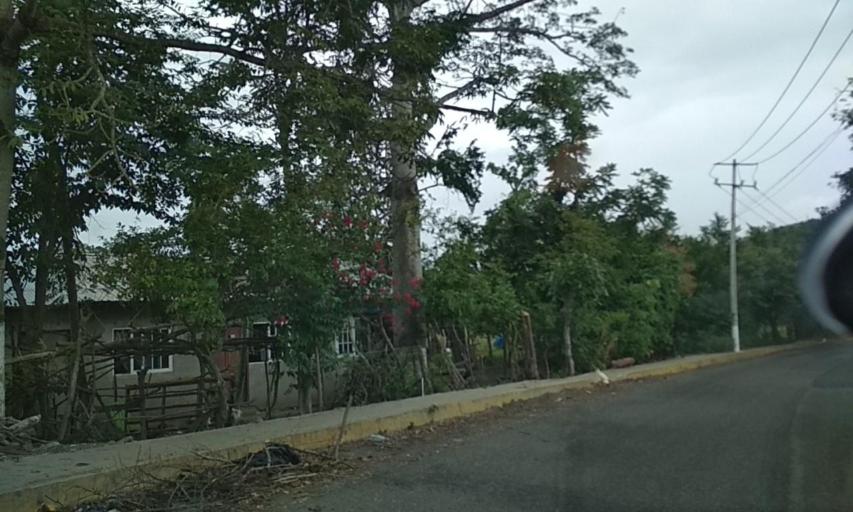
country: MX
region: Veracruz
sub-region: Papantla
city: Residencial Tajin
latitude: 20.6413
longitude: -97.3652
